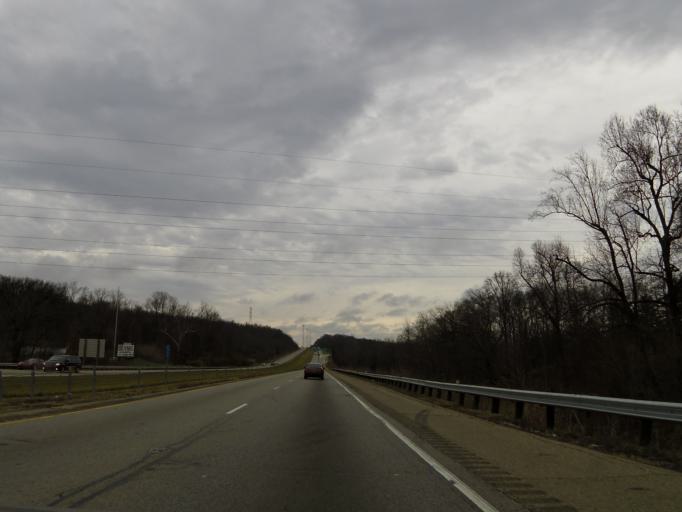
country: US
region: Ohio
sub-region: Hamilton County
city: Grandview
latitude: 39.2261
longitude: -84.7495
